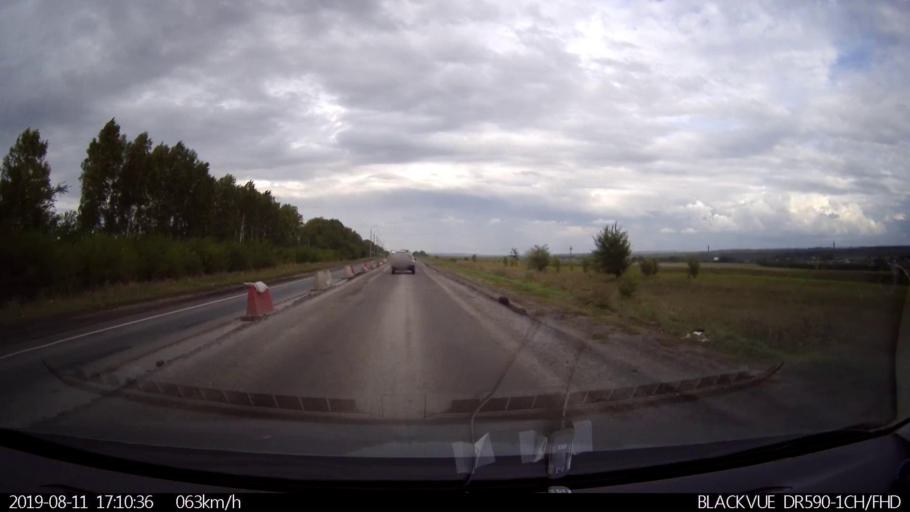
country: RU
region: Ulyanovsk
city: Mayna
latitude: 54.2986
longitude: 47.8753
